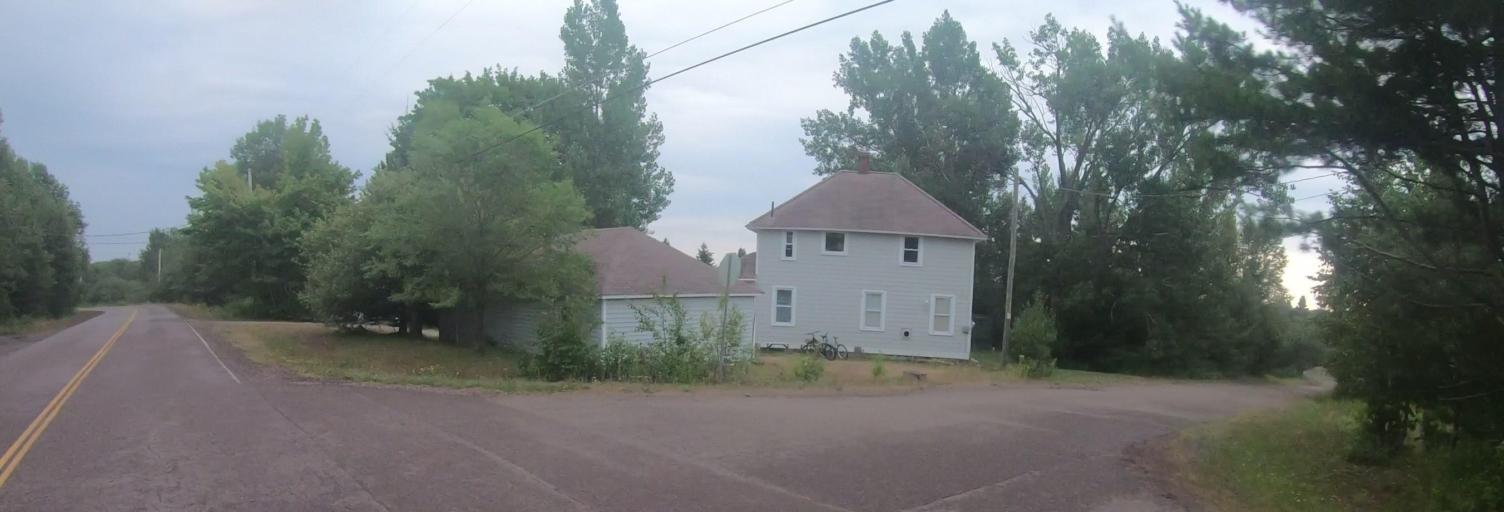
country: US
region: Michigan
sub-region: Houghton County
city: Laurium
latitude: 47.2995
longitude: -88.3552
